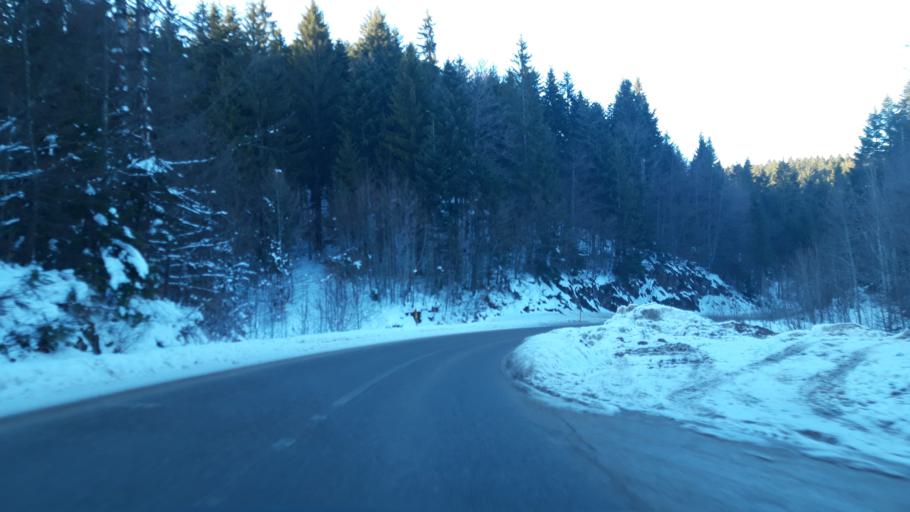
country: BA
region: Republika Srpska
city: Vlasenica
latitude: 44.1454
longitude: 18.9396
